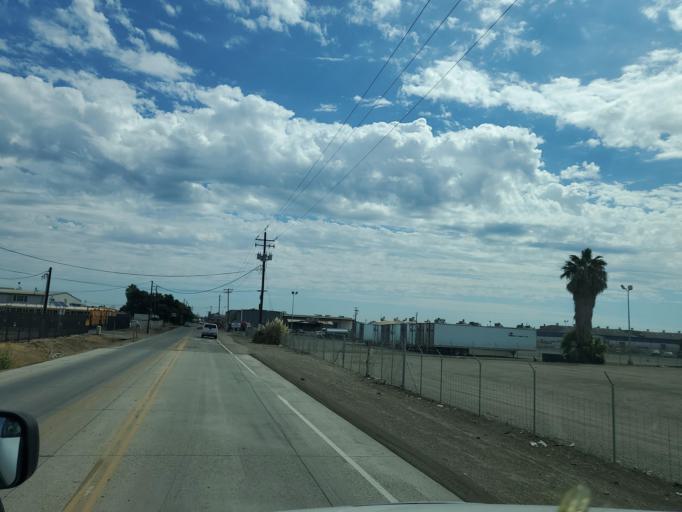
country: US
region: California
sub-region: San Joaquin County
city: Stockton
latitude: 37.9375
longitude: -121.3174
